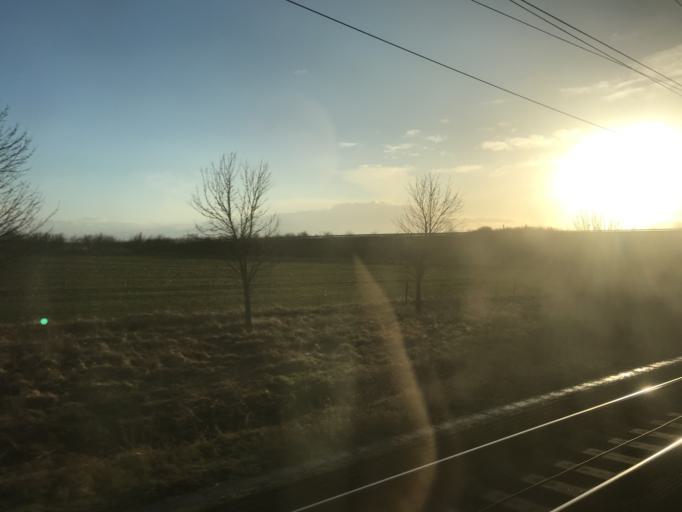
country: DE
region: Saxony-Anhalt
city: Hassel
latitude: 52.6006
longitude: 11.9626
